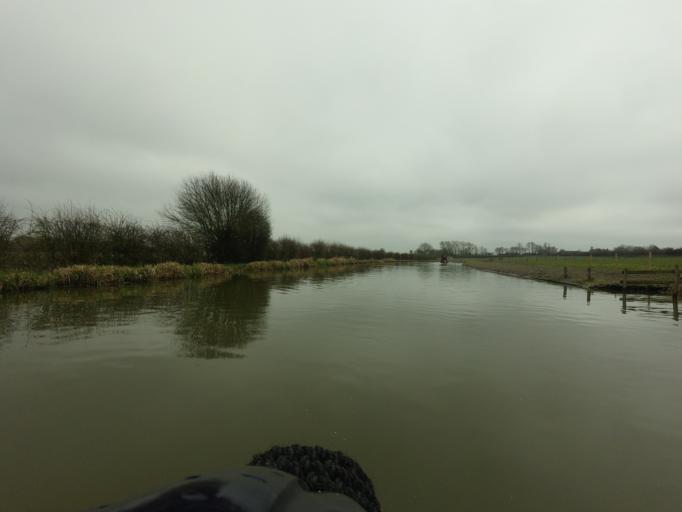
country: GB
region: England
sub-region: Central Bedfordshire
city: Leighton Buzzard
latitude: 51.8967
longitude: -0.6690
